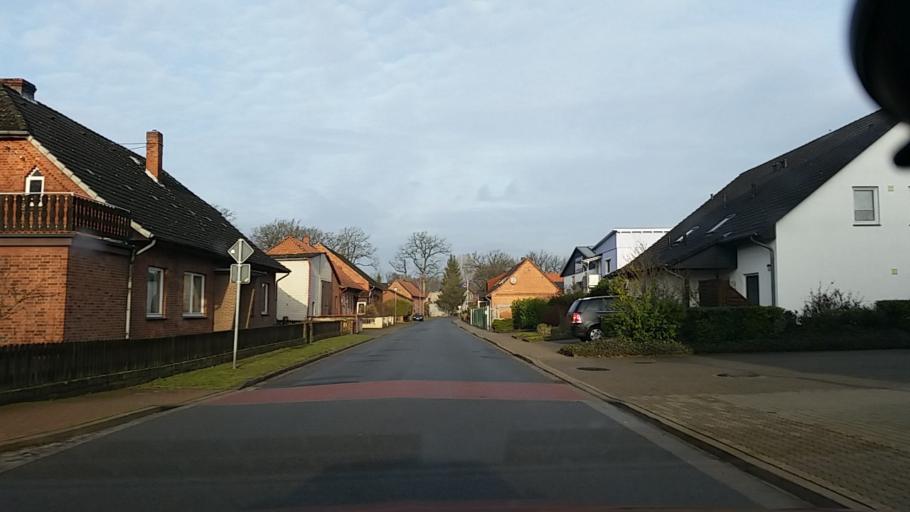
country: DE
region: Lower Saxony
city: Luder
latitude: 52.8070
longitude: 10.6670
